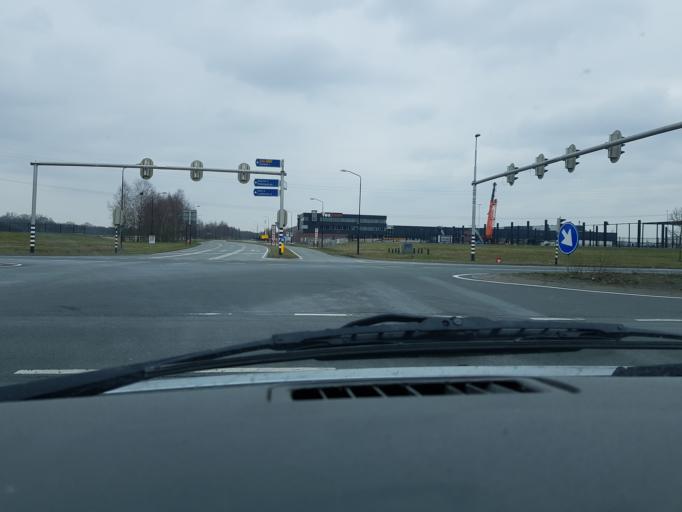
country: NL
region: North Brabant
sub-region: Gemeente Oss
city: Berghem
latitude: 51.7356
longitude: 5.5713
